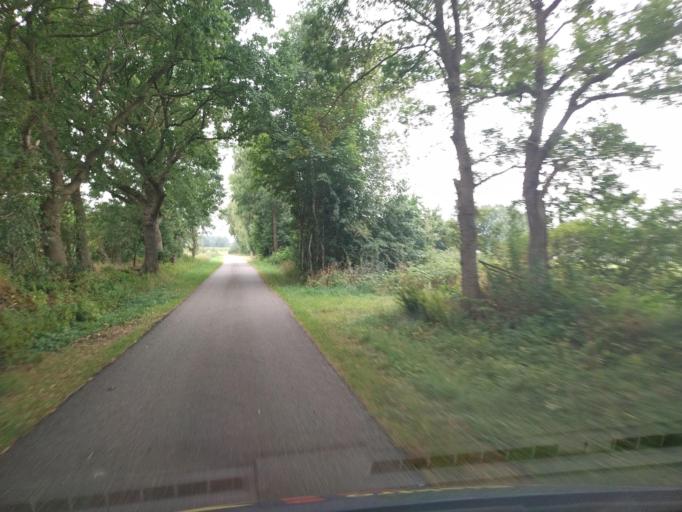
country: DE
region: Schleswig-Holstein
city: Borm
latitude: 54.4067
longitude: 9.3966
